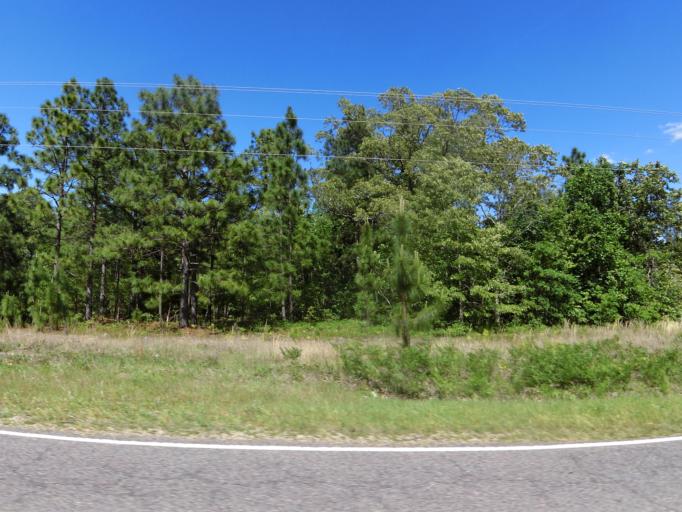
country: US
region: South Carolina
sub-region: Barnwell County
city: Williston
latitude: 33.4549
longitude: -81.4945
